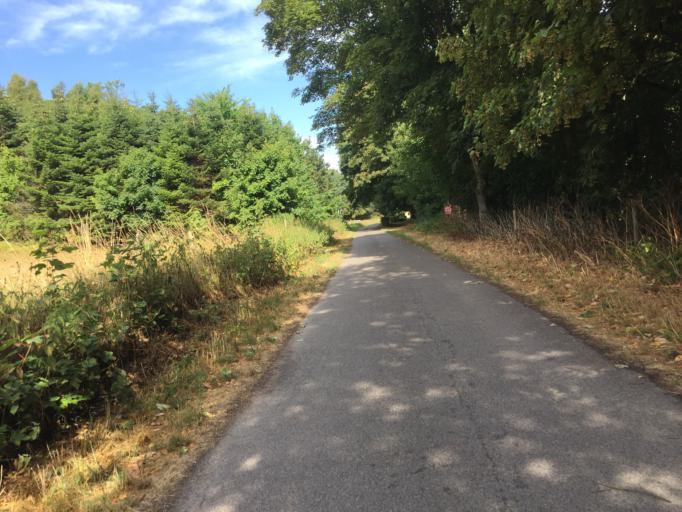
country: DK
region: Central Jutland
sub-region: Samso Kommune
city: Tranebjerg
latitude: 55.9496
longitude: 10.4320
